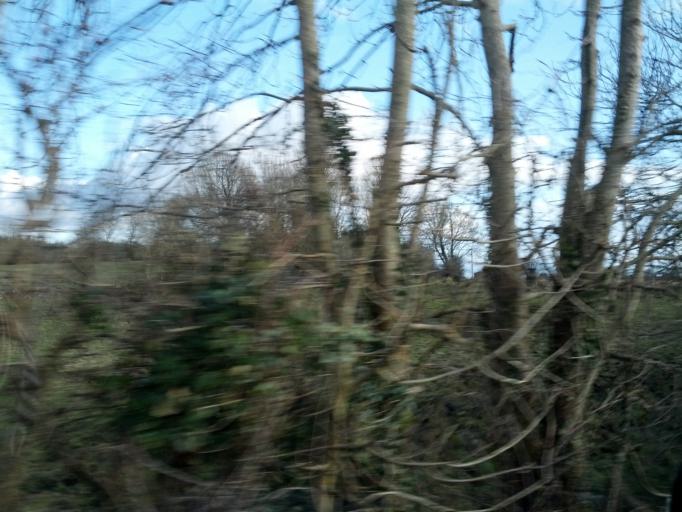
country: IE
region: Connaught
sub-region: County Galway
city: Athenry
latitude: 53.3910
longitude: -8.6227
